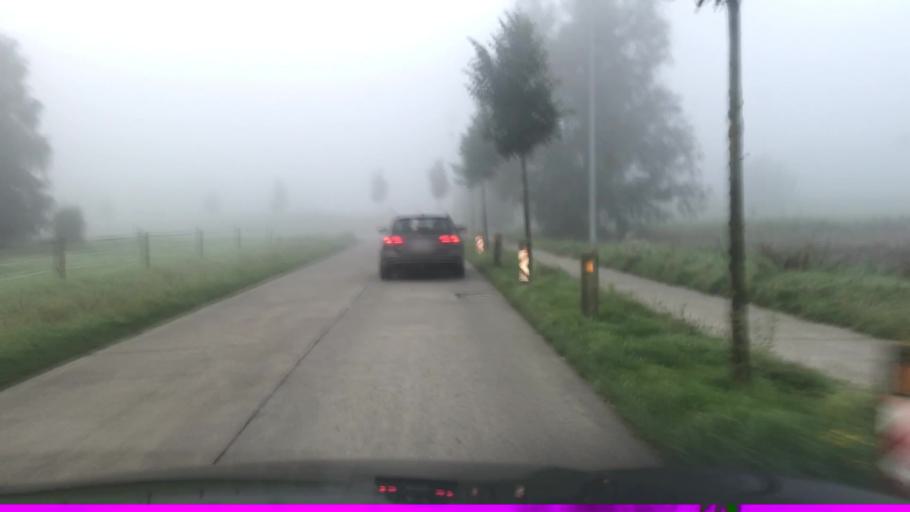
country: BE
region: Flanders
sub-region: Provincie Oost-Vlaanderen
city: Lochristi
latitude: 51.0920
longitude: 3.8604
